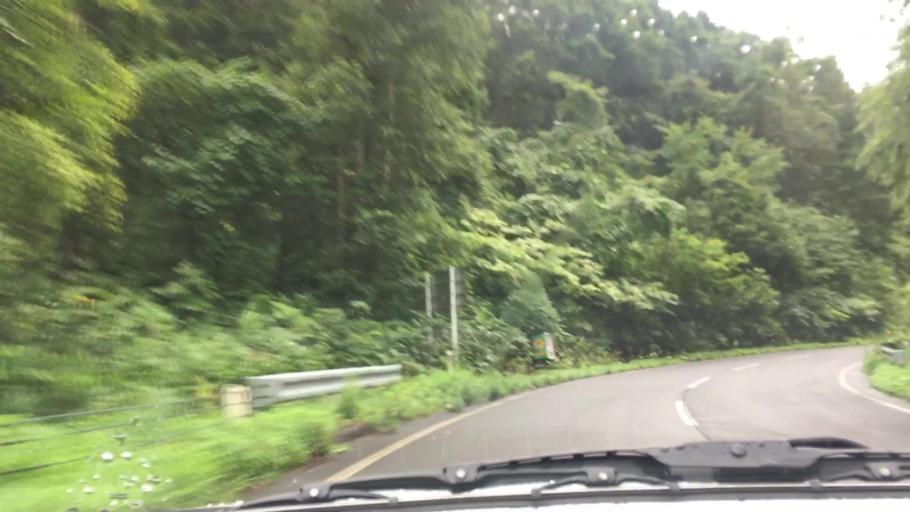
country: JP
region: Hokkaido
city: Niseko Town
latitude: 42.6271
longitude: 140.7234
